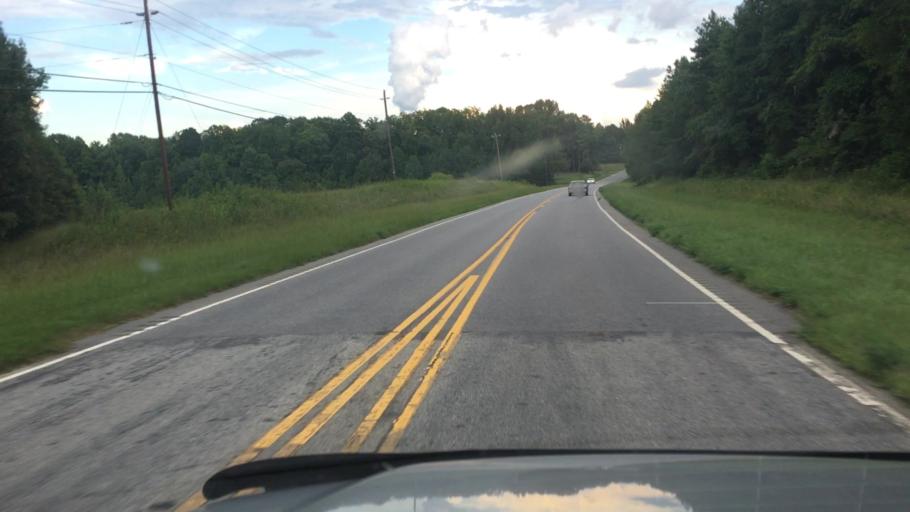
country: US
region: South Carolina
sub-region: Spartanburg County
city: Mayo
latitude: 35.1411
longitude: -81.8135
